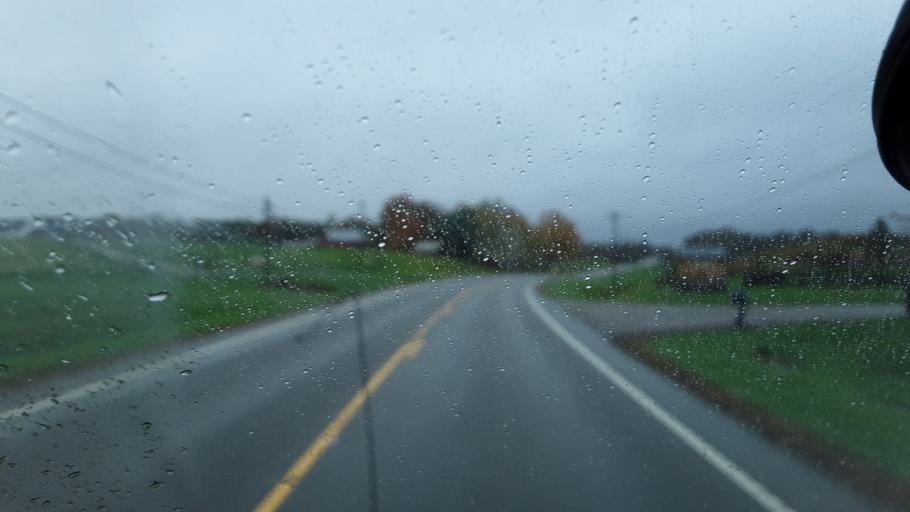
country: US
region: Ohio
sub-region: Morrow County
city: Mount Gilead
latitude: 40.5337
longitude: -82.7662
